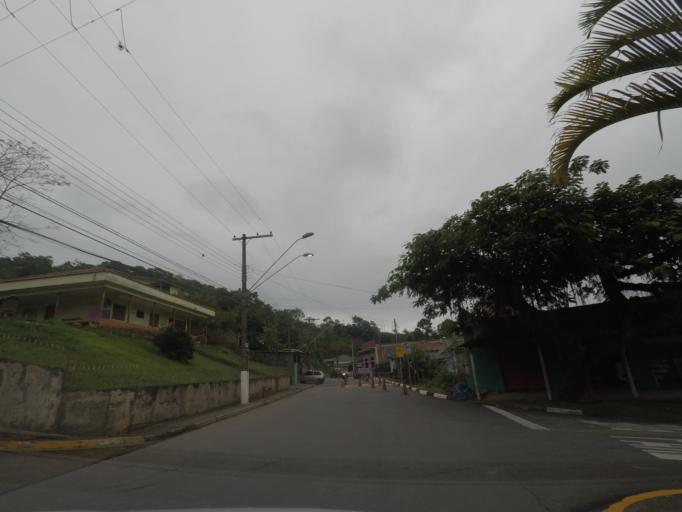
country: BR
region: Sao Paulo
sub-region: Cajati
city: Cajati
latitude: -24.7220
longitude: -48.1067
